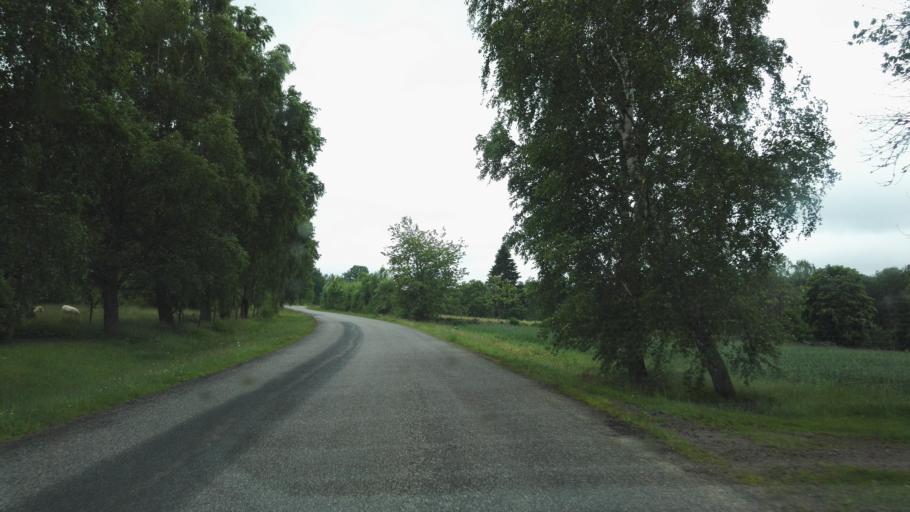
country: SE
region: Joenkoeping
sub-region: Vetlanda Kommun
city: Landsbro
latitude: 57.2538
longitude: 14.8310
